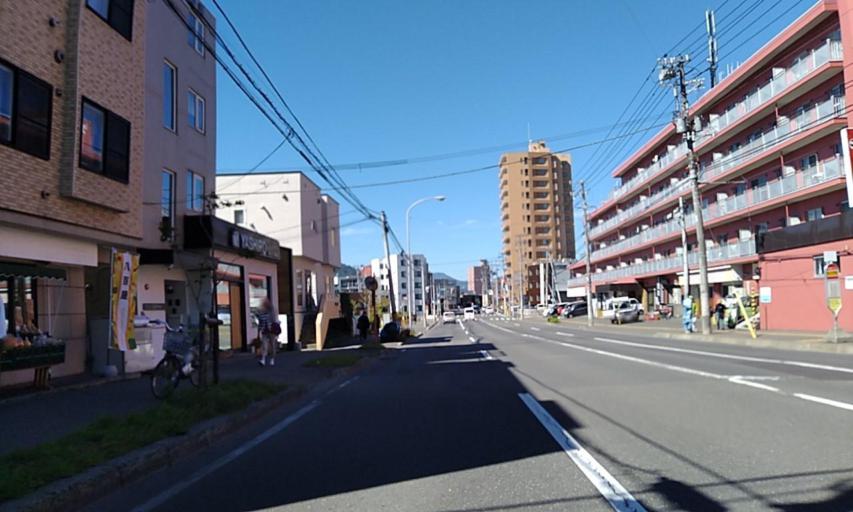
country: JP
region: Hokkaido
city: Sapporo
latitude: 43.0129
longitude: 141.3719
